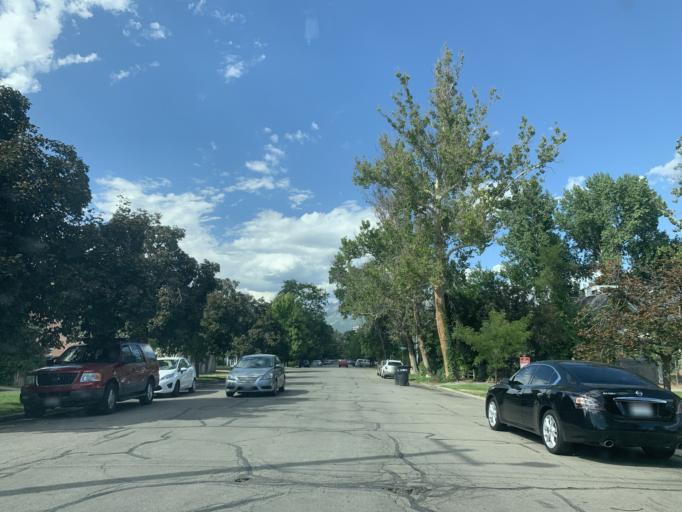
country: US
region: Utah
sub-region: Utah County
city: Provo
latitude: 40.2371
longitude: -111.6516
